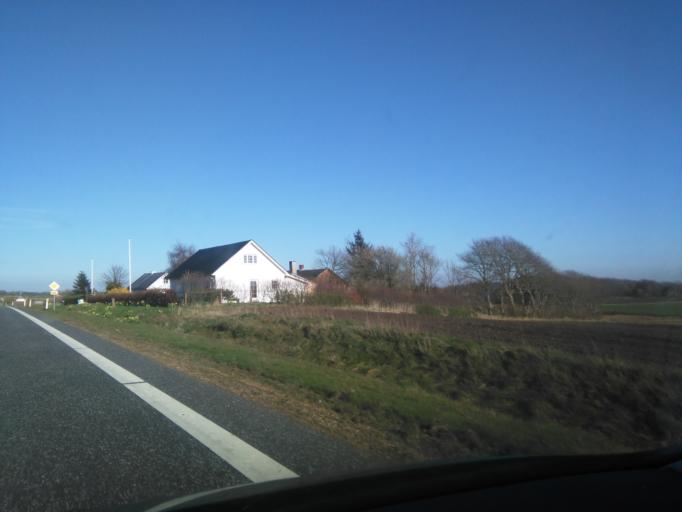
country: DK
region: Central Jutland
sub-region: Ringkobing-Skjern Kommune
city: Videbaek
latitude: 56.0888
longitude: 8.5620
